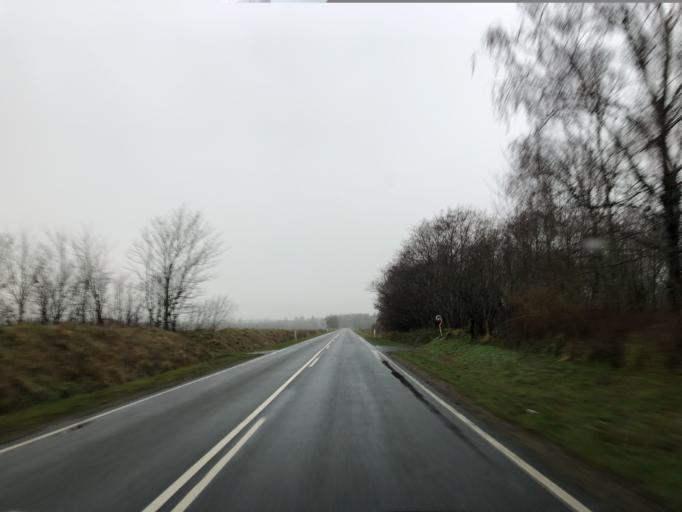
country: DK
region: Central Jutland
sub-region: Holstebro Kommune
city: Ulfborg
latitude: 56.1987
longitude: 8.4075
